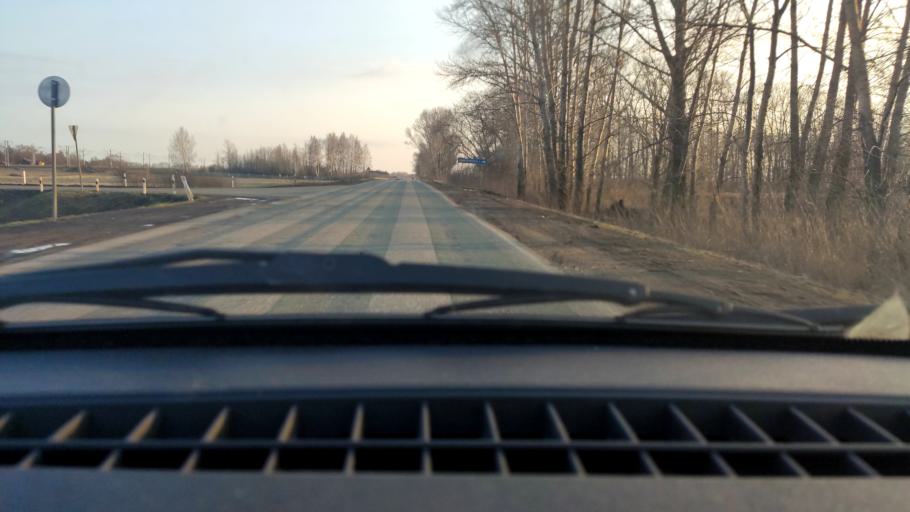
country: RU
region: Bashkortostan
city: Chishmy
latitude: 54.4515
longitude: 55.2484
